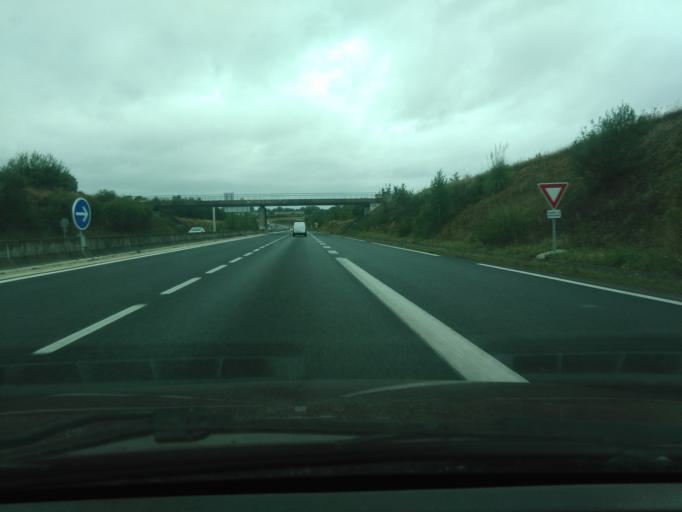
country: FR
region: Pays de la Loire
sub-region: Departement de la Vendee
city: La Ferriere
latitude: 46.6734
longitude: -1.3625
